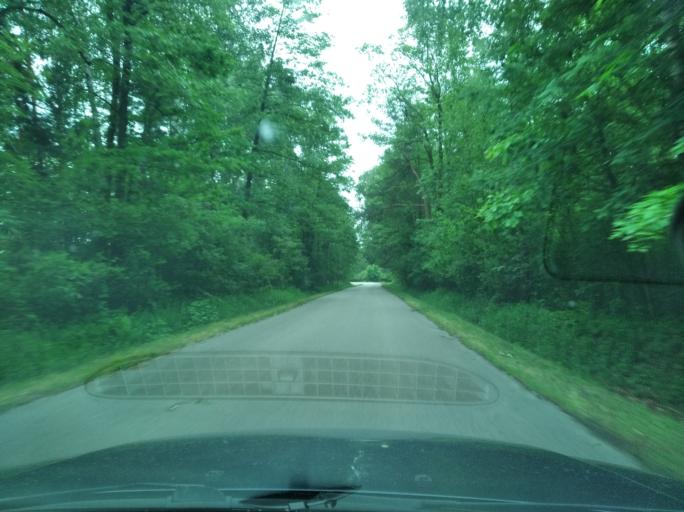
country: PL
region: Subcarpathian Voivodeship
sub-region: Powiat kolbuszowski
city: Niwiska
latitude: 50.2144
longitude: 21.6467
